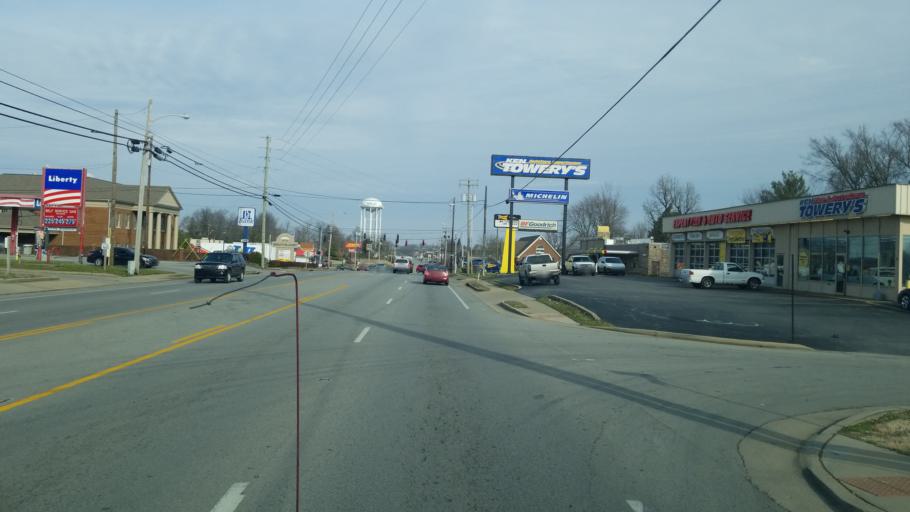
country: US
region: Kentucky
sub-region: Boyle County
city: Danville
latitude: 37.6272
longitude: -84.7747
